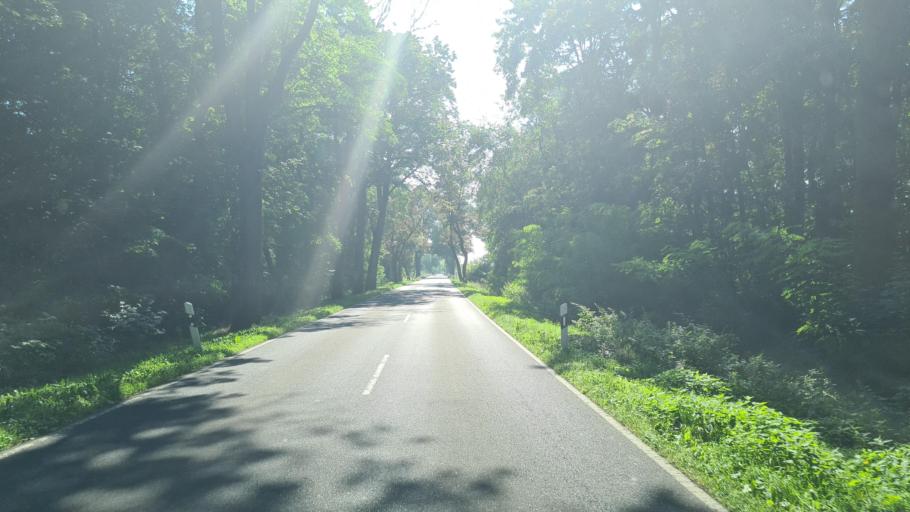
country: DE
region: Brandenburg
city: Friesack
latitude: 52.7816
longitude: 12.5948
